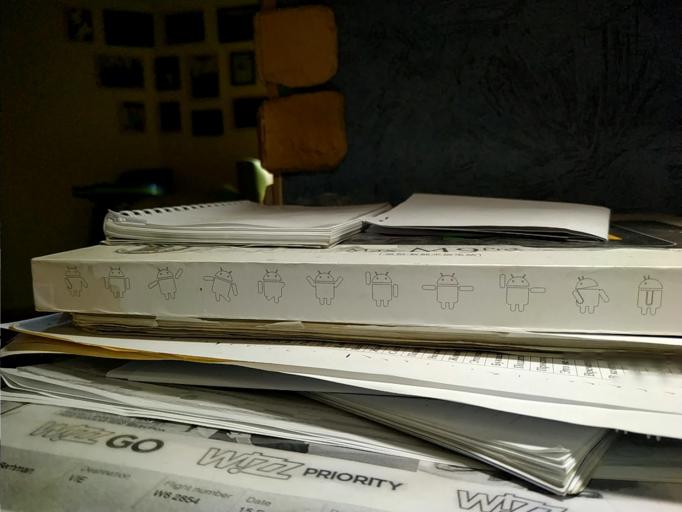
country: RU
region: Novgorod
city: Poddor'ye
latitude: 57.5267
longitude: 30.9088
